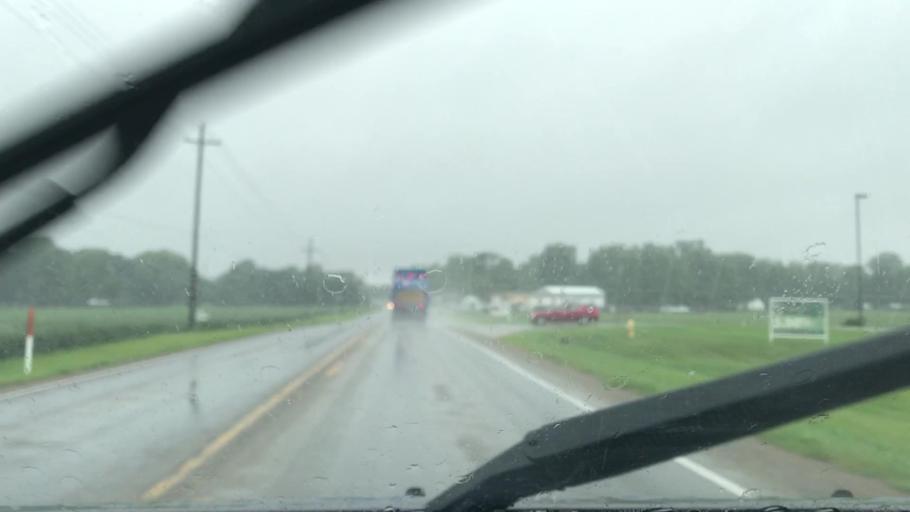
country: US
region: Indiana
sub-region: Hamilton County
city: Sheridan
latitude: 40.1275
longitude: -86.2047
